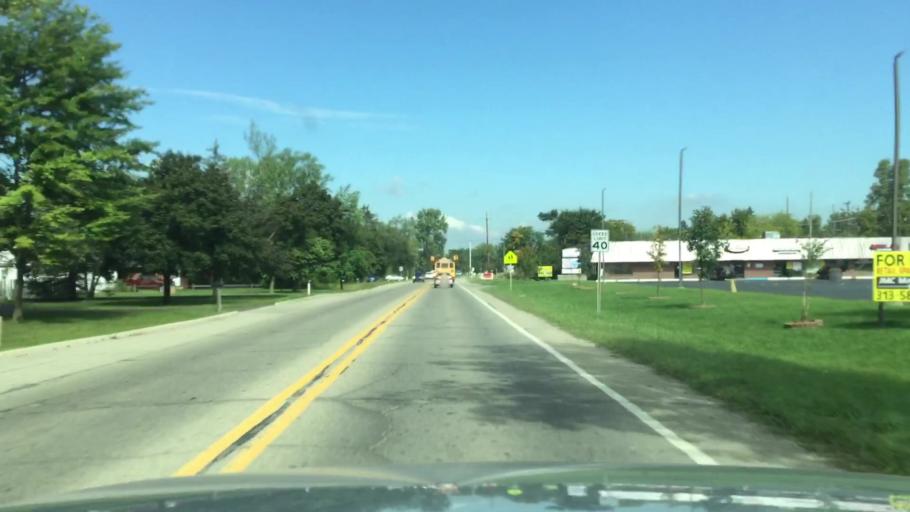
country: US
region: Michigan
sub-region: Wayne County
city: Belleville
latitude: 42.1950
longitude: -83.4844
